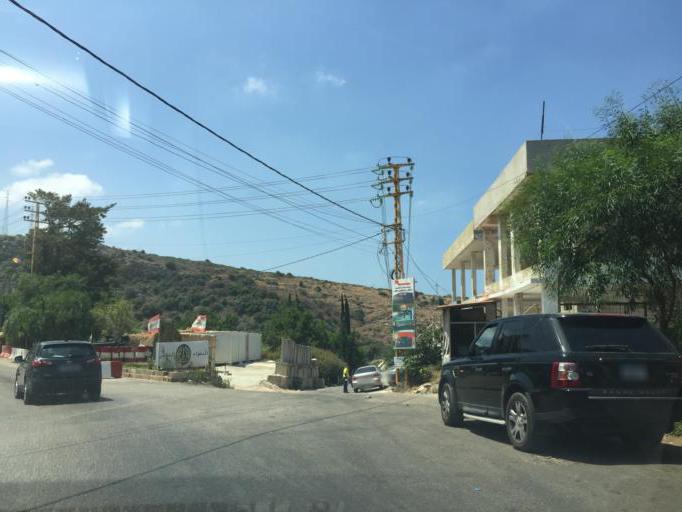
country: LB
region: Mont-Liban
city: Beit ed Dine
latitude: 33.7067
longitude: 35.4498
